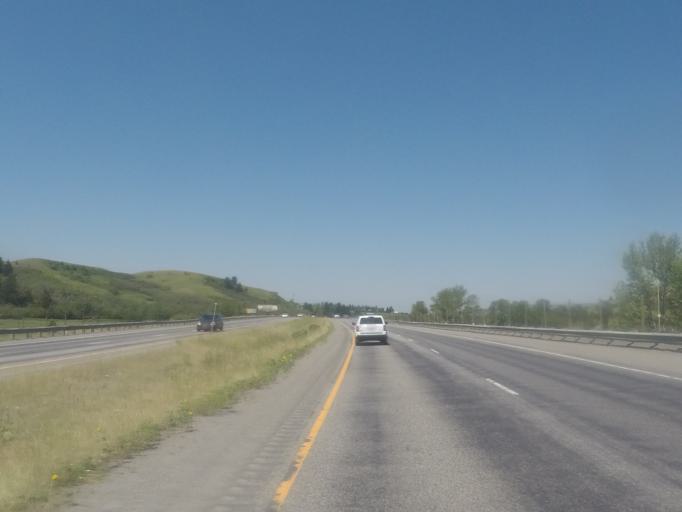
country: US
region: Montana
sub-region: Gallatin County
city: Bozeman
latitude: 45.6462
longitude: -110.9313
